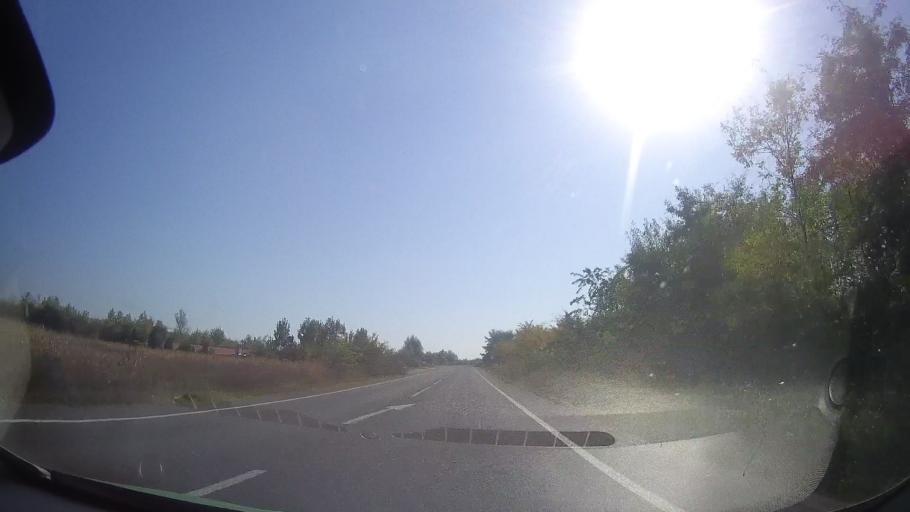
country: RO
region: Timis
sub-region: Comuna Costeiu
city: Costeiu
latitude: 45.7389
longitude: 21.8425
